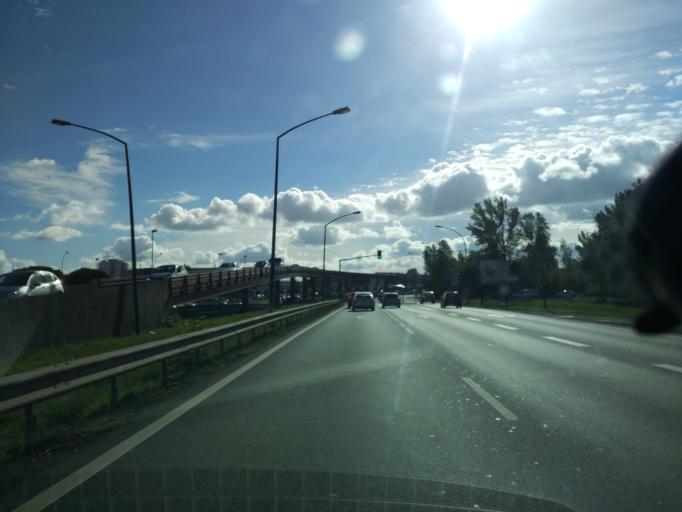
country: FR
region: Aquitaine
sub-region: Departement de la Gironde
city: Le Bouscat
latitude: 44.8714
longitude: -0.5661
